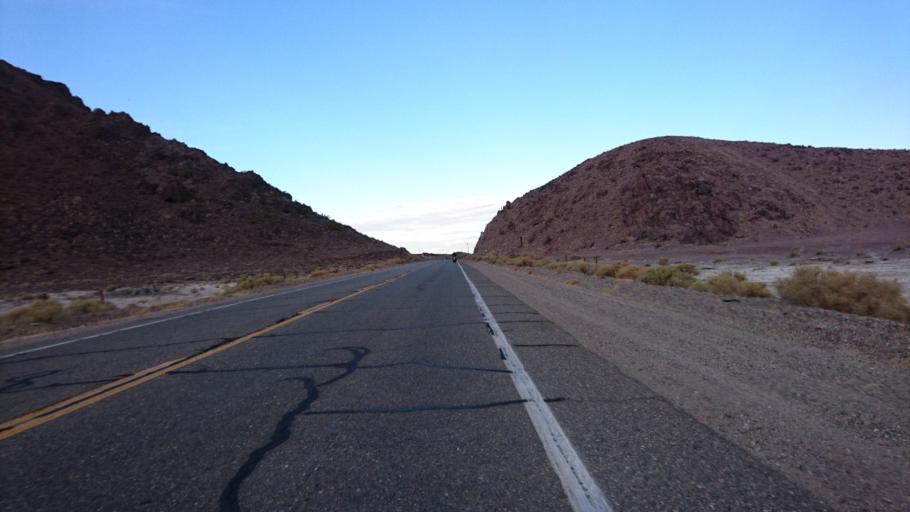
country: US
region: California
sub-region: San Bernardino County
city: Barstow
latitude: 34.8254
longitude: -116.6765
